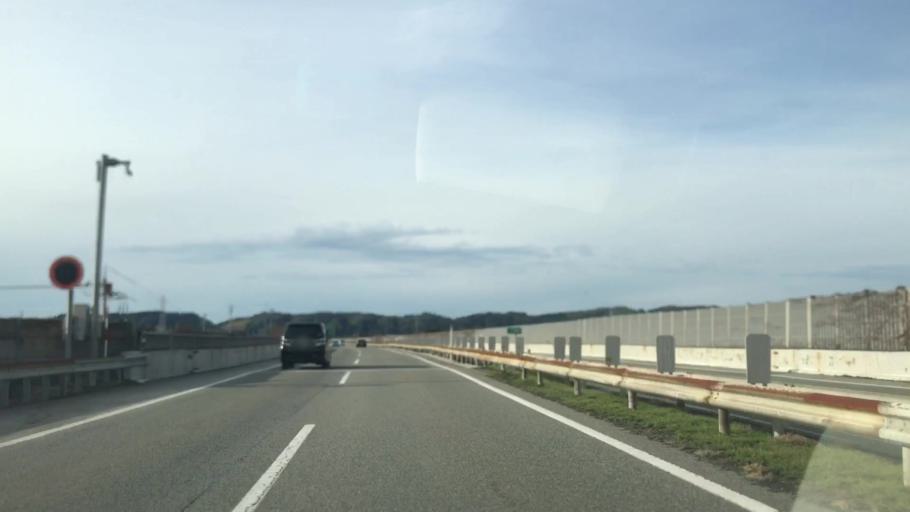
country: JP
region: Toyama
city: Toyama-shi
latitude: 36.6713
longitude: 137.1775
